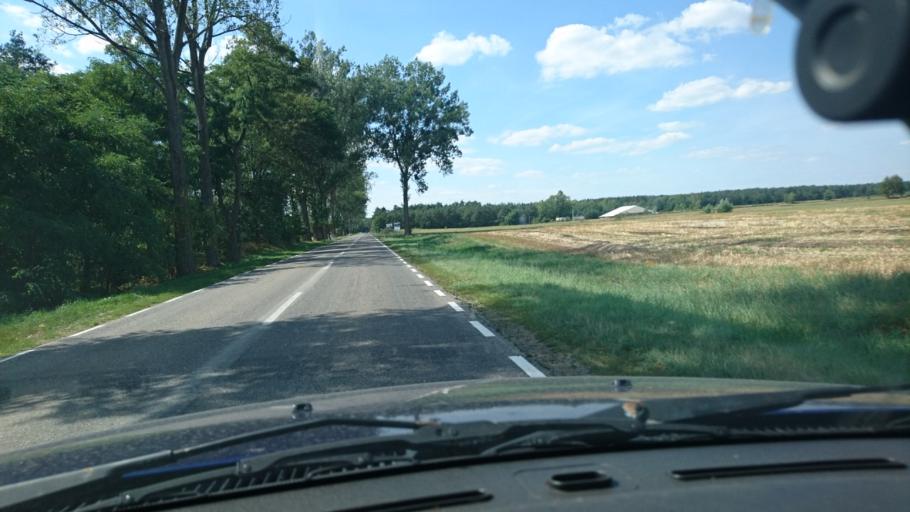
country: PL
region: Greater Poland Voivodeship
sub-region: Powiat ostrowski
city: Odolanow
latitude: 51.5934
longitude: 17.6253
